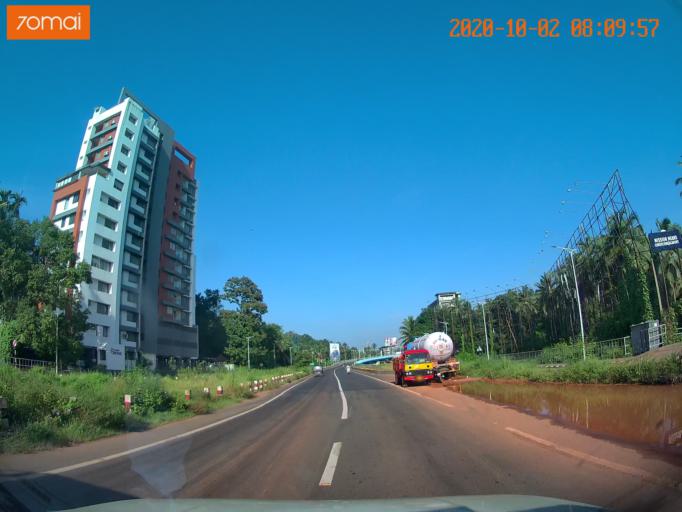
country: IN
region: Kerala
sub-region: Kozhikode
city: Kozhikode
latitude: 11.2634
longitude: 75.8157
